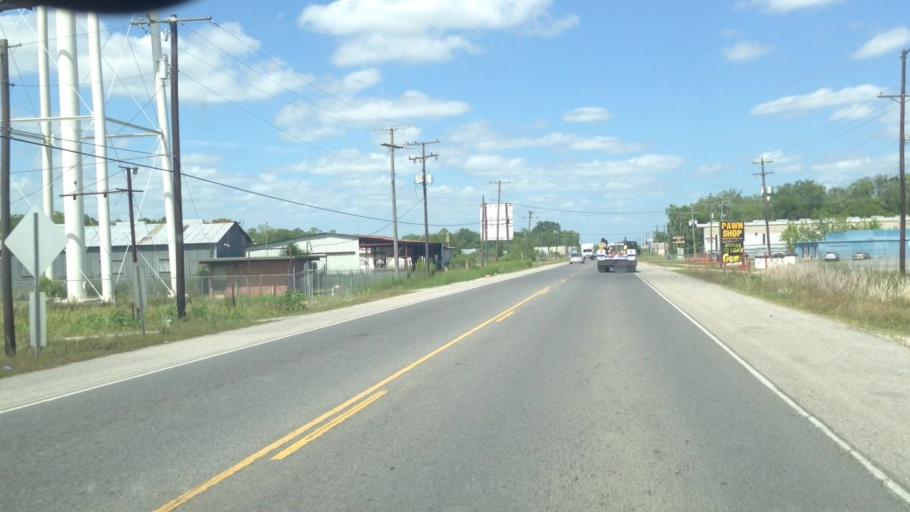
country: US
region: Louisiana
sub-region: Terrebonne Parish
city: Houma
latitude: 29.6477
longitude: -90.6856
